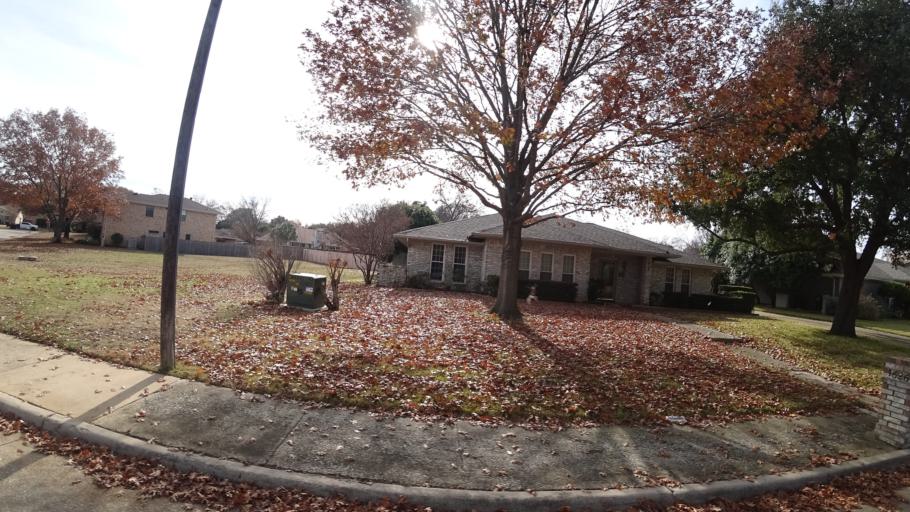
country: US
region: Texas
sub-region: Denton County
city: Highland Village
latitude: 33.0811
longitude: -97.0426
